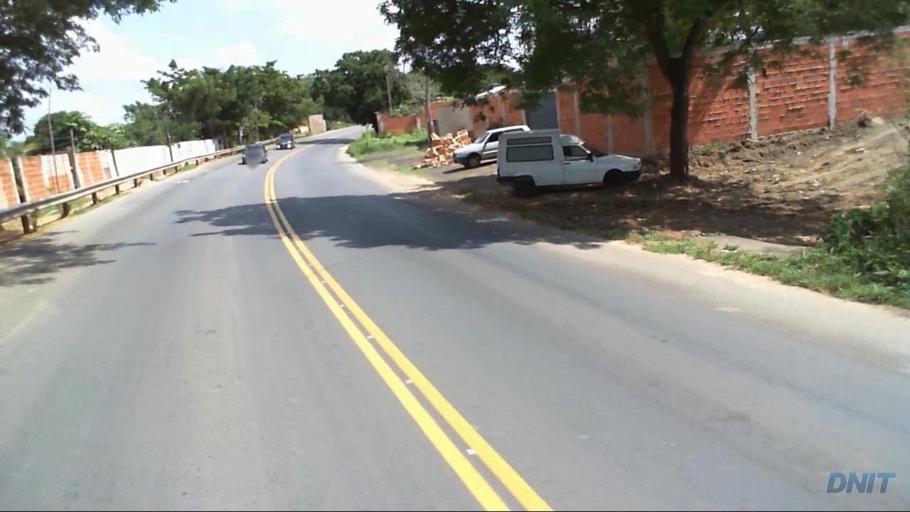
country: BR
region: Minas Gerais
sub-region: Governador Valadares
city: Governador Valadares
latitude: -18.9146
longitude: -41.9998
